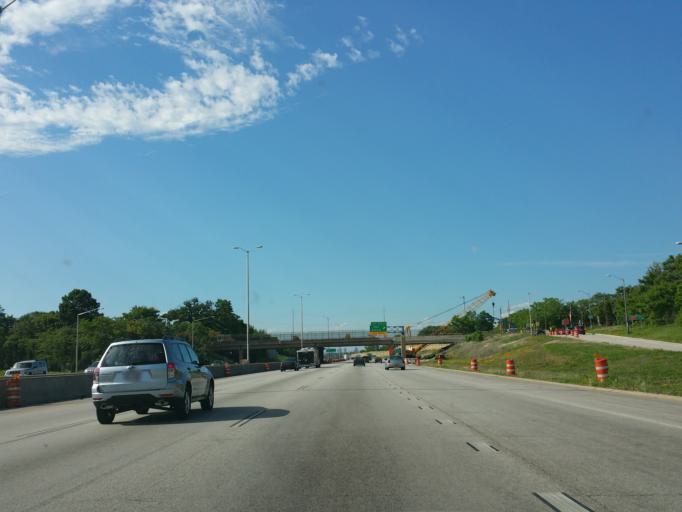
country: US
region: Wisconsin
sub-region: Milwaukee County
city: Saint Francis
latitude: 42.9718
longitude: -87.9153
